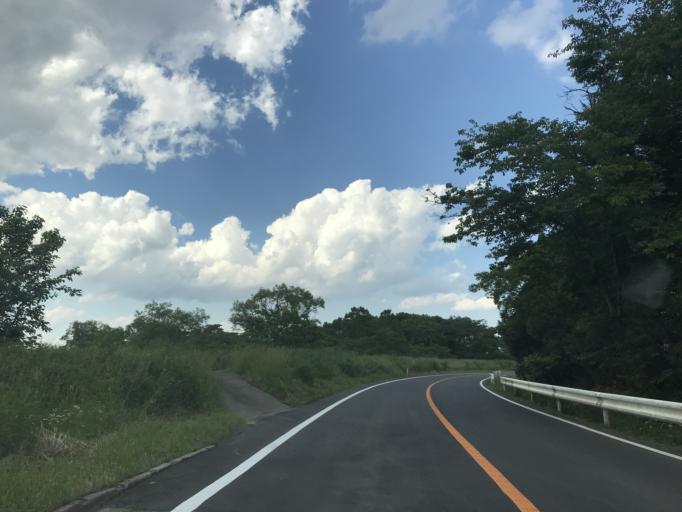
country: JP
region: Miyagi
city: Wakuya
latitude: 38.6573
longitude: 141.2121
